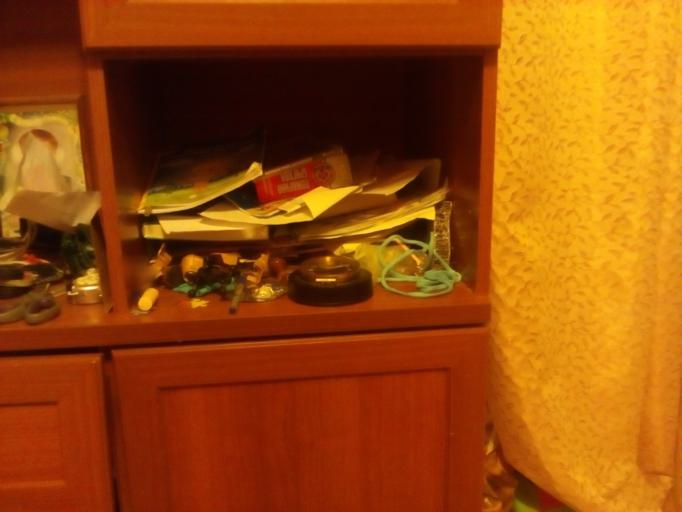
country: RU
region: Jaroslavl
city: Yaroslavl
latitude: 57.6832
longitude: 39.7991
